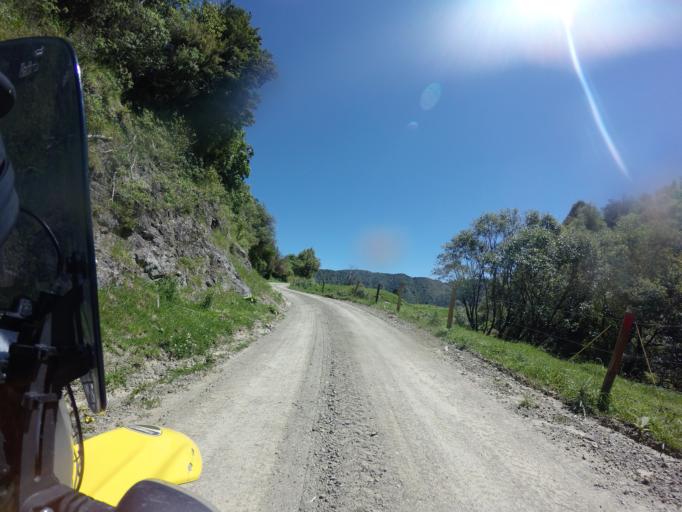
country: NZ
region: Bay of Plenty
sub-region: Opotiki District
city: Opotiki
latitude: -38.4047
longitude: 177.4520
